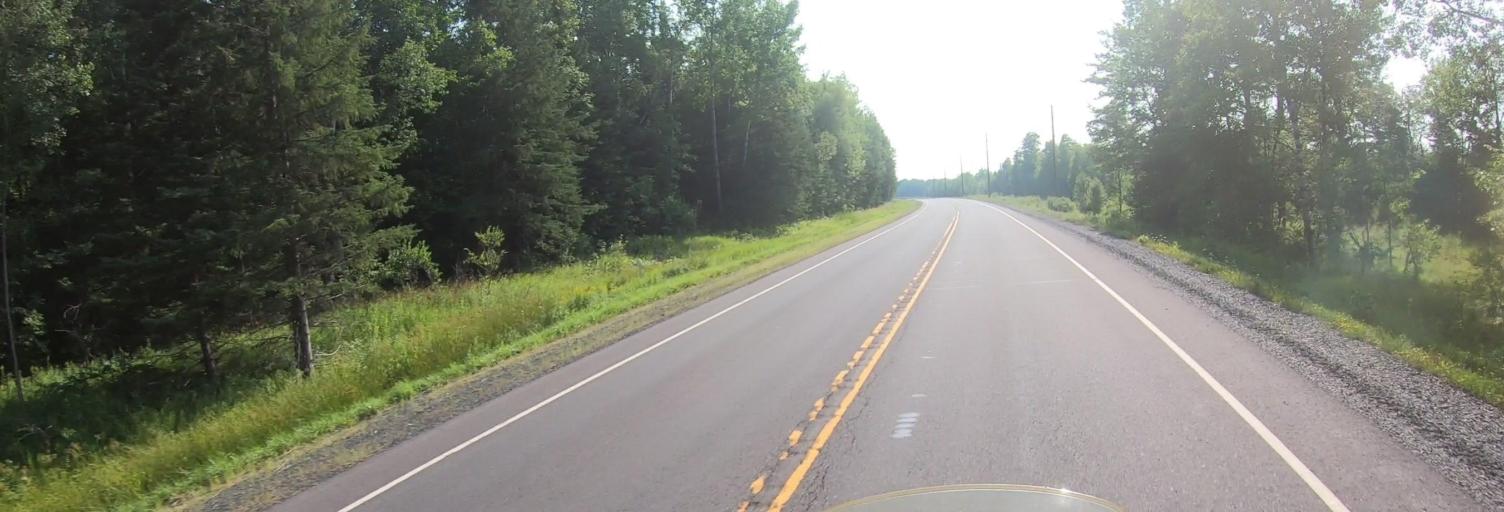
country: US
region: Wisconsin
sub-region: Iron County
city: Hurley
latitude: 46.3757
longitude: -90.3867
